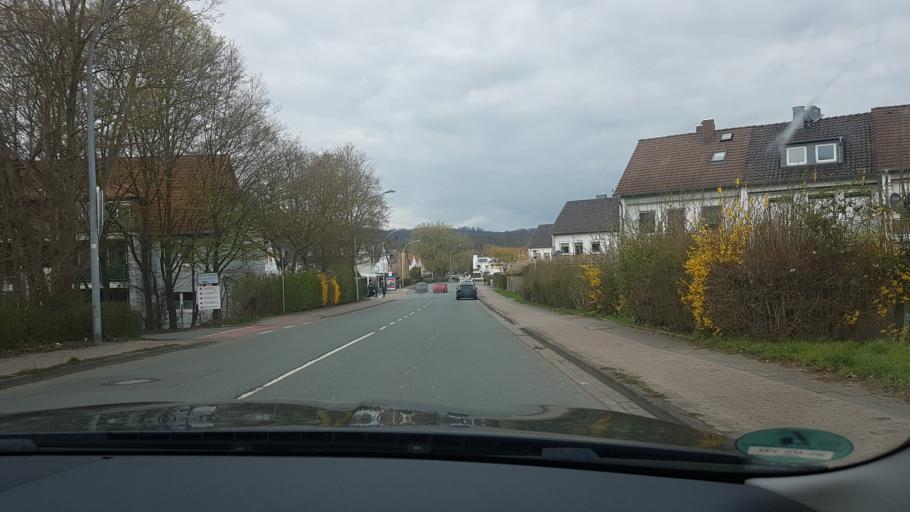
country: DE
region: Lower Saxony
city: Hameln
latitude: 52.1203
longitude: 9.3390
